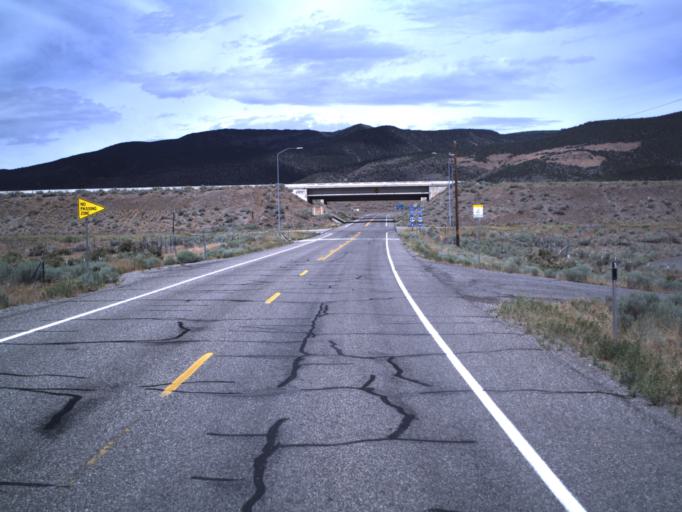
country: US
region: Utah
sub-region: Sevier County
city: Monroe
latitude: 38.6244
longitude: -112.2238
